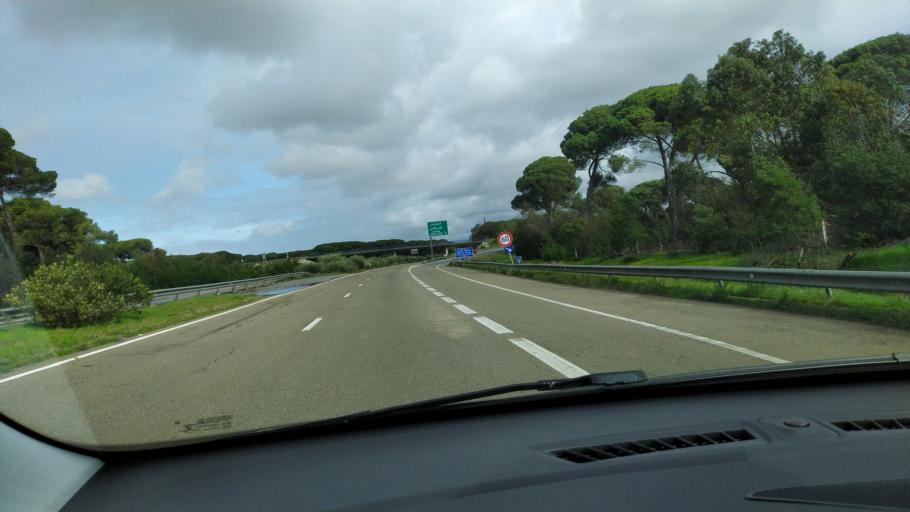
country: MA
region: Tanger-Tetouan
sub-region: Larache
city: Larache
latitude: 35.1383
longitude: -6.1465
